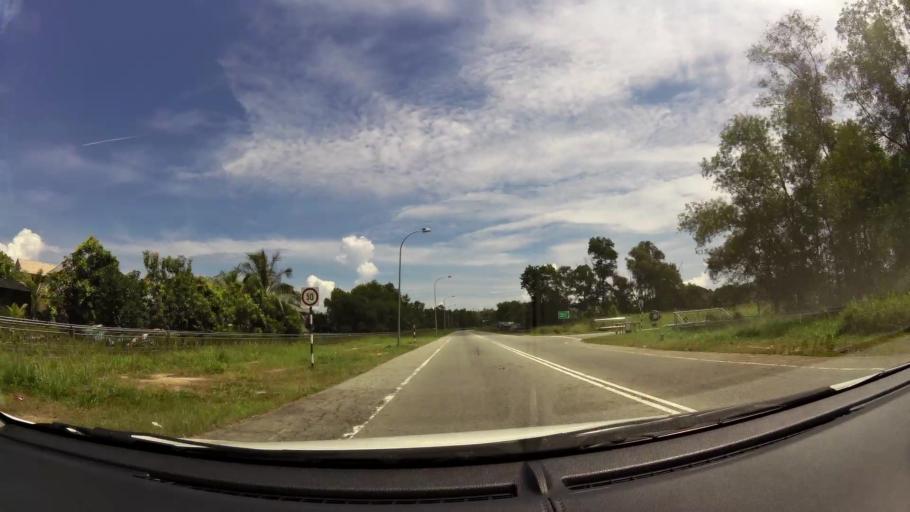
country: BN
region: Brunei and Muara
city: Bandar Seri Begawan
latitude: 4.9557
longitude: 114.9046
